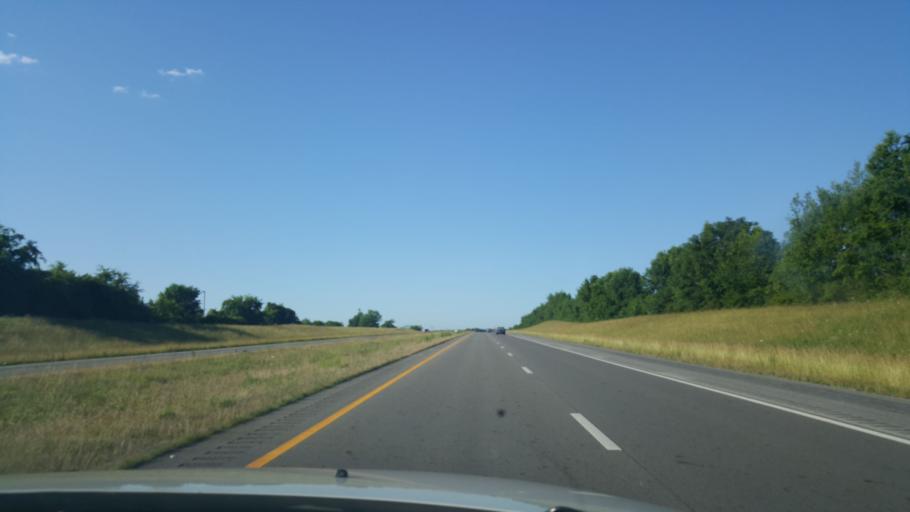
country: US
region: Tennessee
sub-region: Maury County
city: Columbia
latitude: 35.6067
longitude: -87.1217
